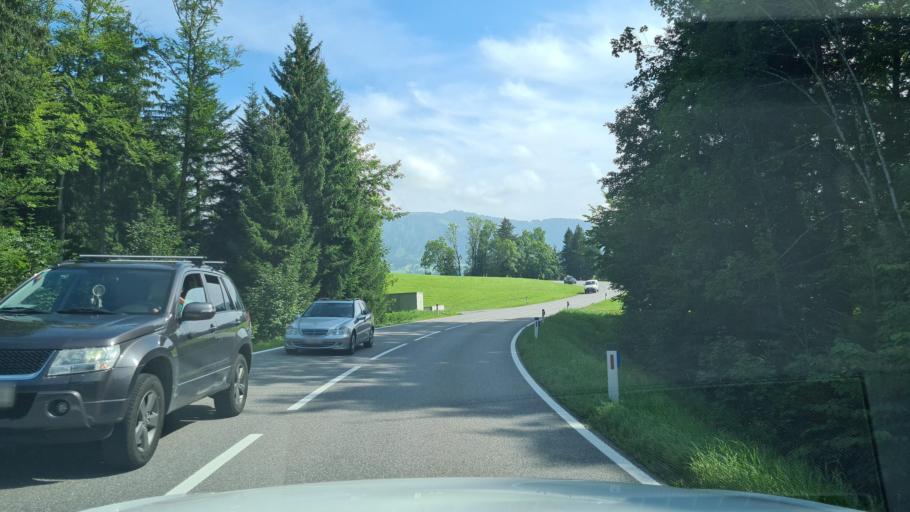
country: AT
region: Vorarlberg
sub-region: Politischer Bezirk Bregenz
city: Egg
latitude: 47.4505
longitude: 9.8966
